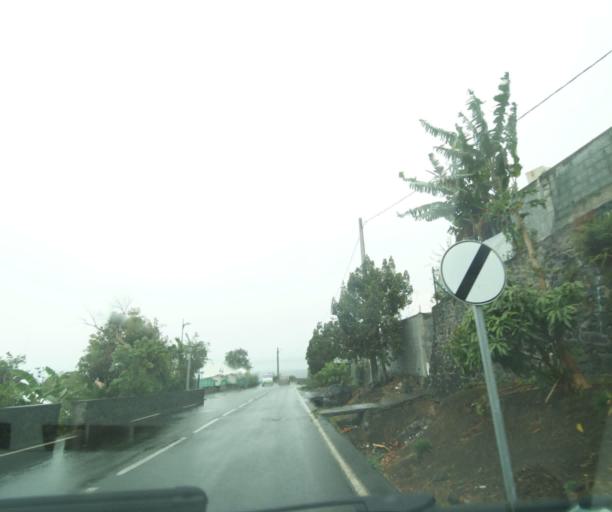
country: RE
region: Reunion
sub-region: Reunion
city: Saint-Paul
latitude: -21.0294
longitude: 55.2851
